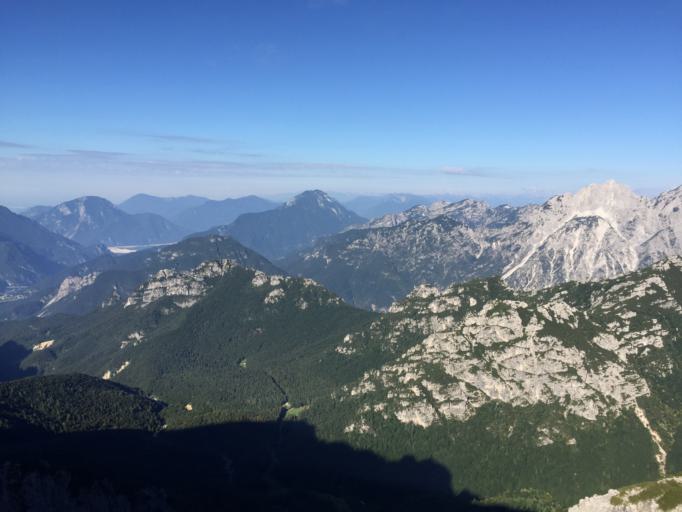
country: IT
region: Friuli Venezia Giulia
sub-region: Provincia di Udine
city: Pontebba
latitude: 46.4731
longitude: 13.2437
